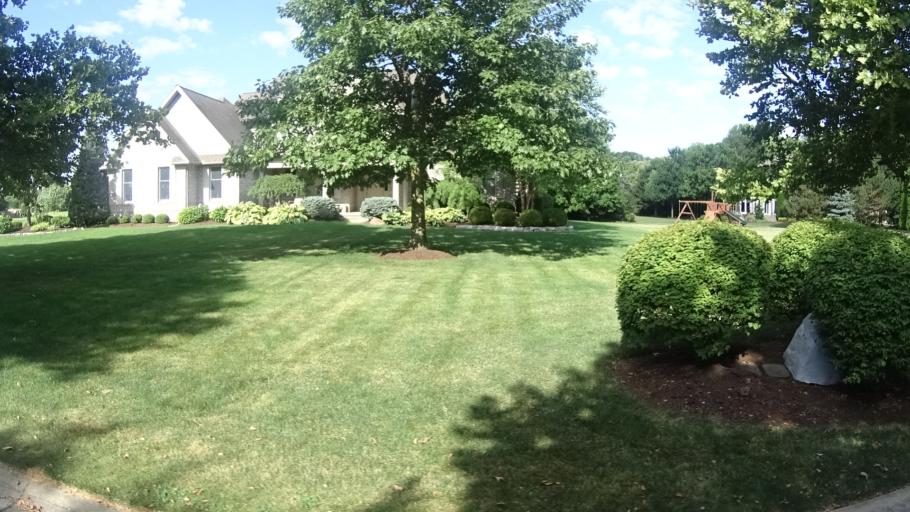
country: US
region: Ohio
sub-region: Erie County
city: Sandusky
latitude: 41.4157
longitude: -82.6582
